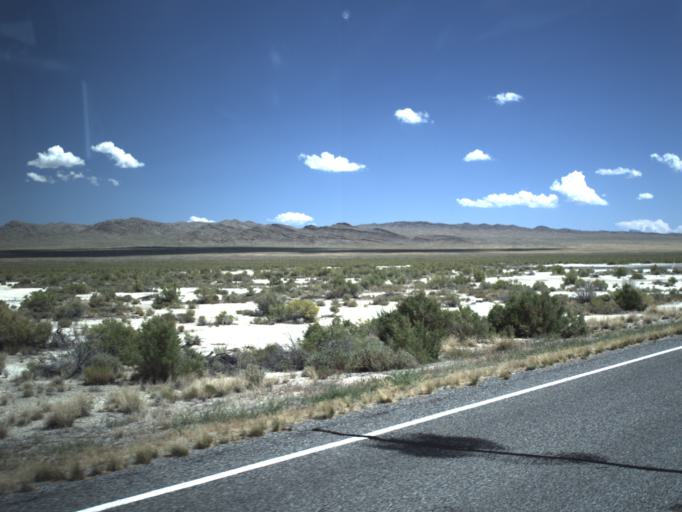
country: US
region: Nevada
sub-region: White Pine County
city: McGill
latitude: 39.0467
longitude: -113.9133
